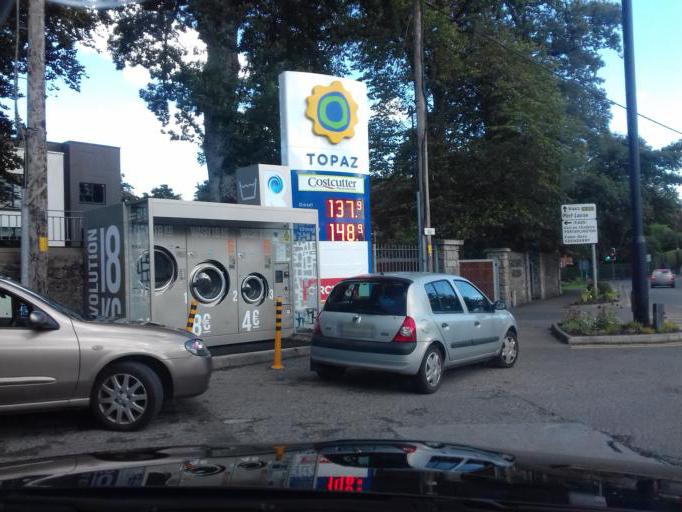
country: IE
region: Leinster
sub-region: Uibh Fhaili
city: Tullamore
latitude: 53.2706
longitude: -7.4914
